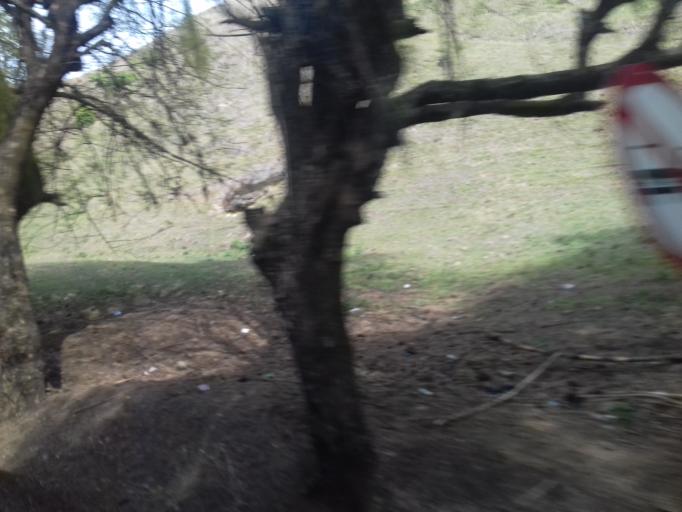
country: CO
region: Antioquia
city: Concordia
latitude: 5.9652
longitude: -75.8441
